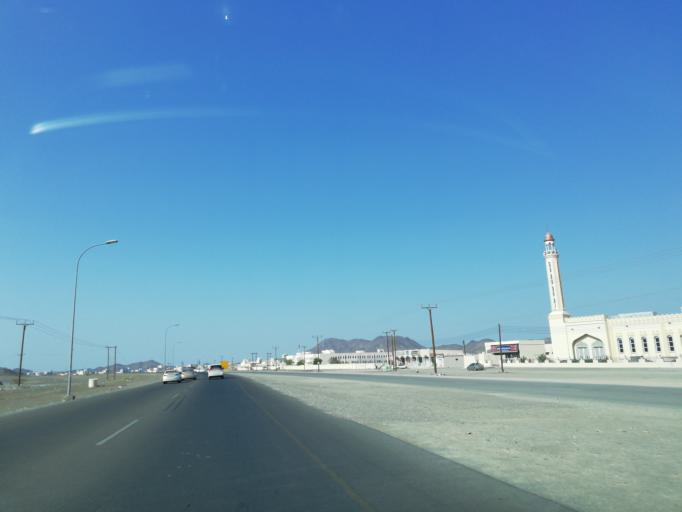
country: OM
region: Ash Sharqiyah
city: Ibra'
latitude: 22.7838
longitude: 58.1441
